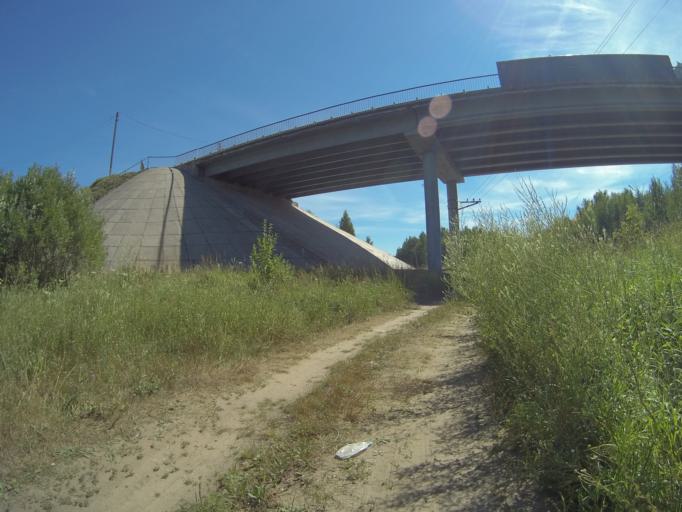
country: RU
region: Vladimir
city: Raduzhnyy
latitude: 56.0634
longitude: 40.3694
